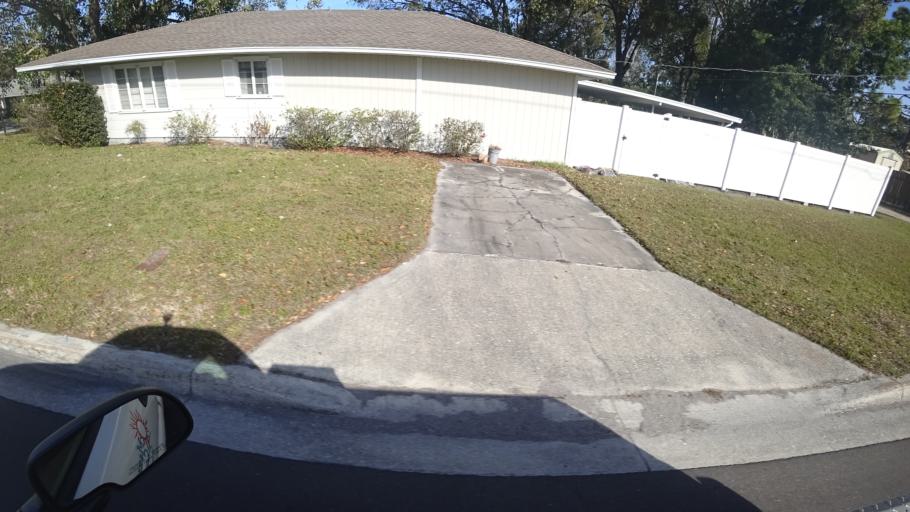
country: US
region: Florida
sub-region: Manatee County
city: Bradenton
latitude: 27.4847
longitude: -82.5913
